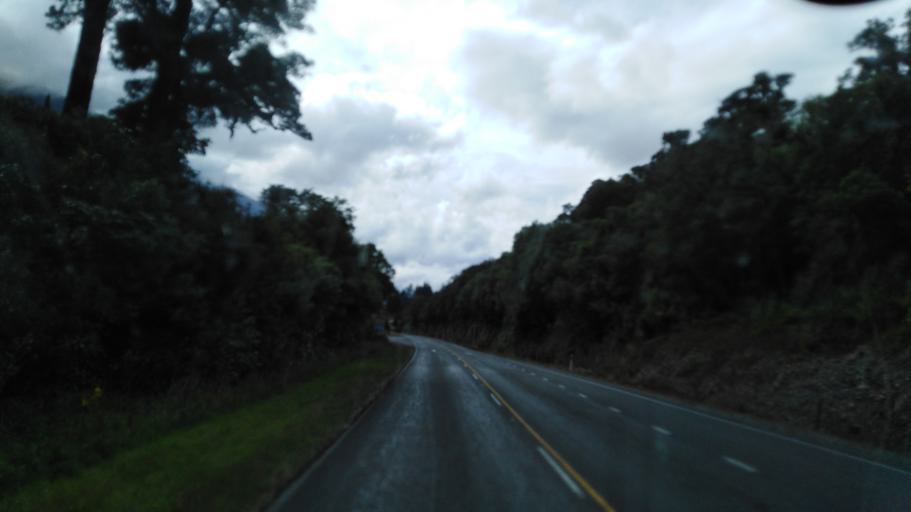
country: NZ
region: West Coast
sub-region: Grey District
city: Greymouth
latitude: -42.7438
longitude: 171.5038
